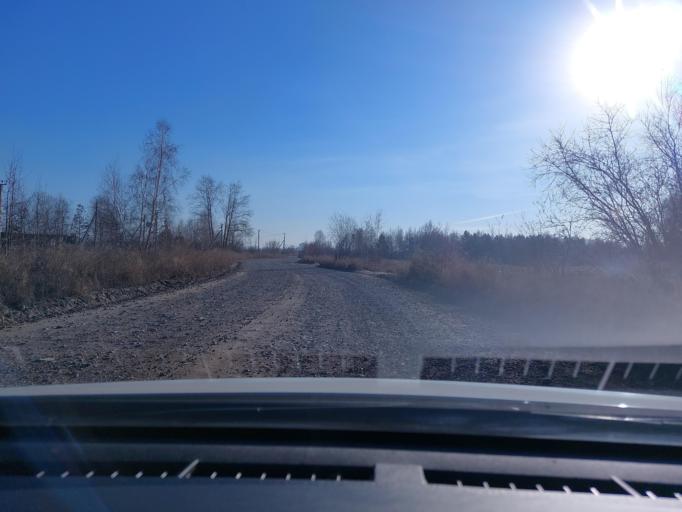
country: RU
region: Irkutsk
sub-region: Irkutskiy Rayon
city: Irkutsk
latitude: 52.3071
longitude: 104.2730
